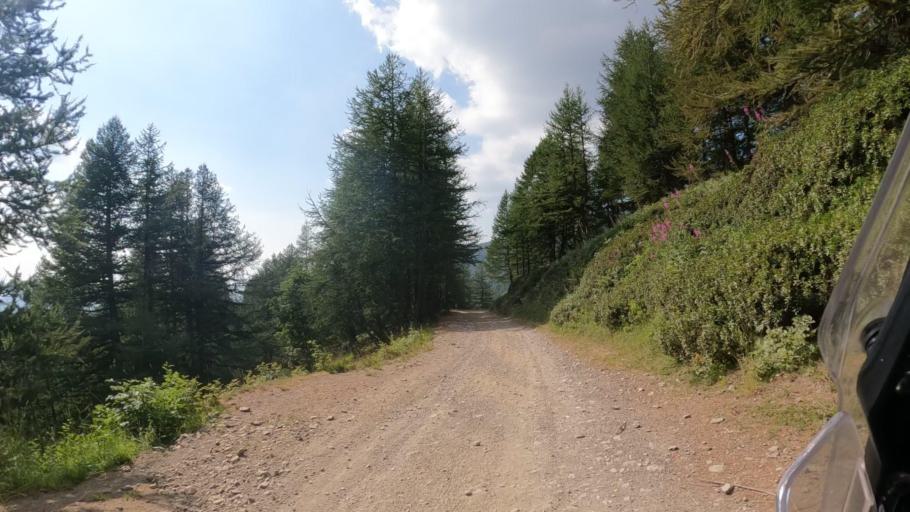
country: IT
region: Piedmont
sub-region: Provincia di Cuneo
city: Briga Alta
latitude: 44.1383
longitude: 7.6769
